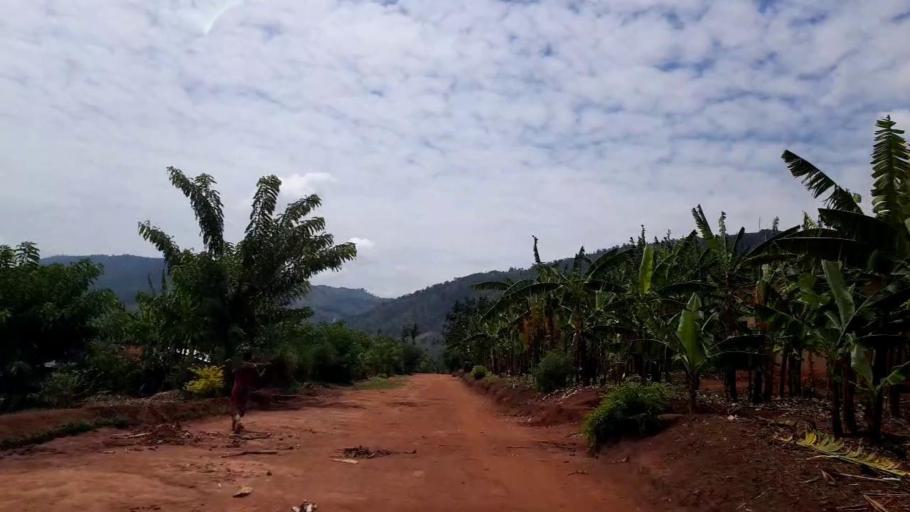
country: RW
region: Northern Province
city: Byumba
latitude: -1.4941
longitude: 30.1954
